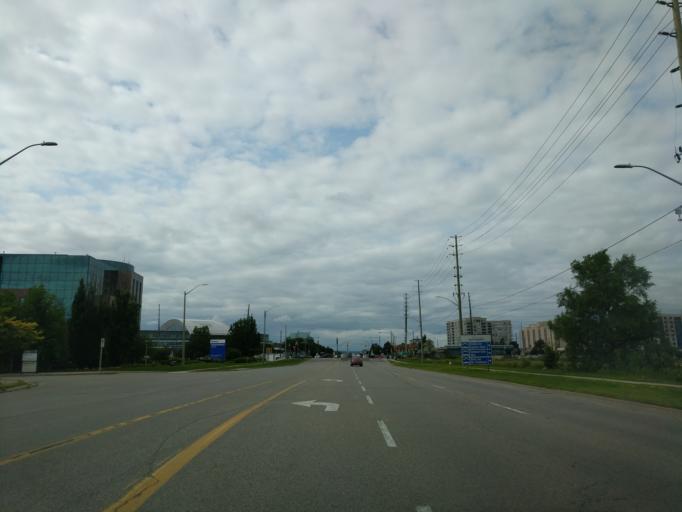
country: CA
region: Ontario
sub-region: York
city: Richmond Hill
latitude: 43.8425
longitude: -79.3818
